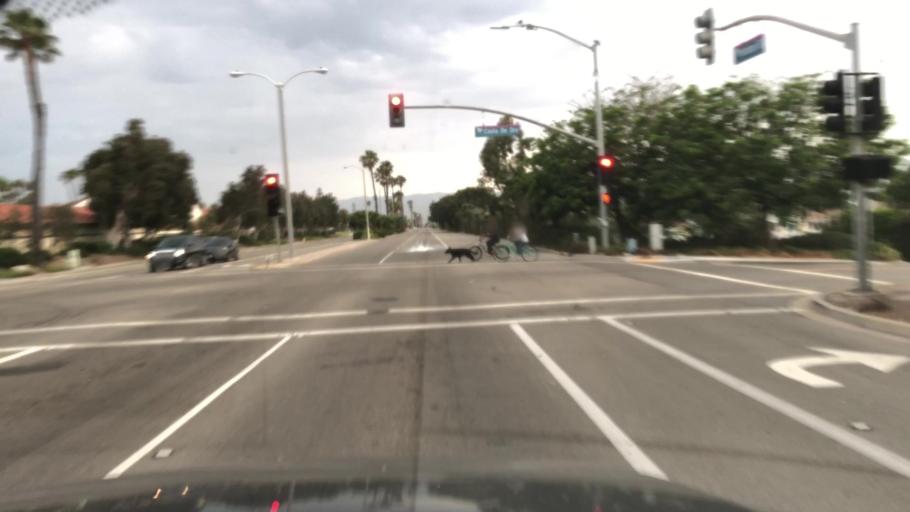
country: US
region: California
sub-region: Ventura County
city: Oxnard Shores
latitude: 34.1799
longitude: -119.2326
